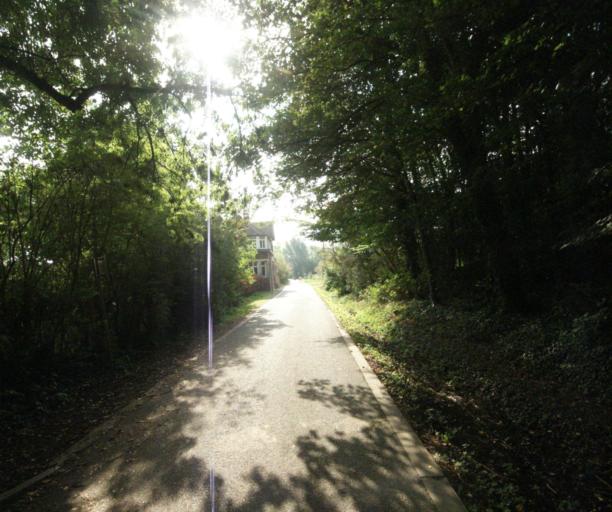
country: FR
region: Nord-Pas-de-Calais
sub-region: Departement du Nord
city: Forest-sur-Marque
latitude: 50.6386
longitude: 3.1681
